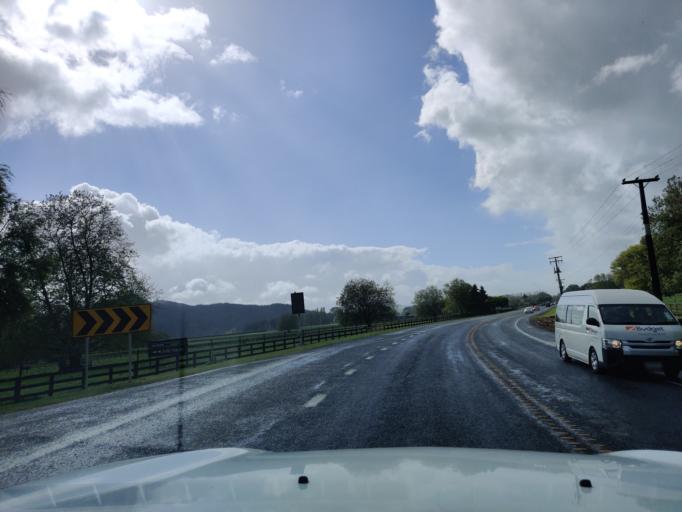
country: NZ
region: Waikato
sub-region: Waipa District
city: Cambridge
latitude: -37.9069
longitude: 175.5280
